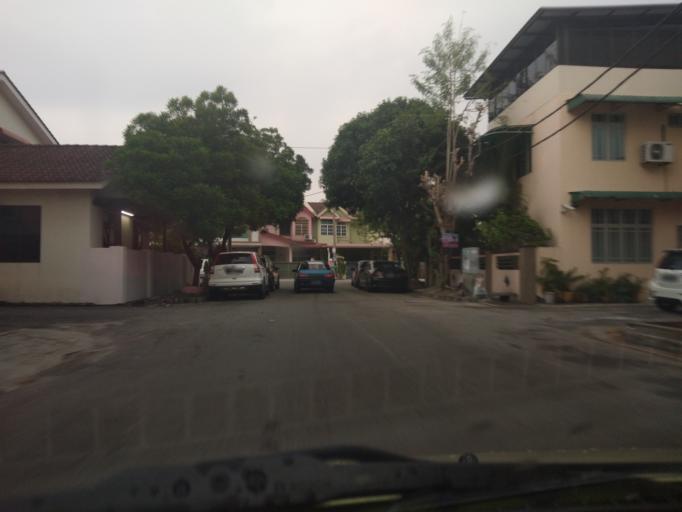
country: MY
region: Penang
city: Permatang Kuching
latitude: 5.4368
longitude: 100.3809
